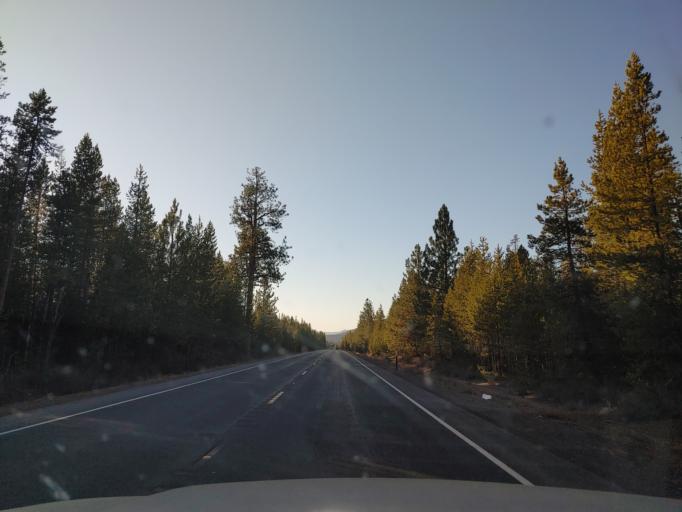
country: US
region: Oregon
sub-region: Deschutes County
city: La Pine
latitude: 43.3929
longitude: -121.8136
